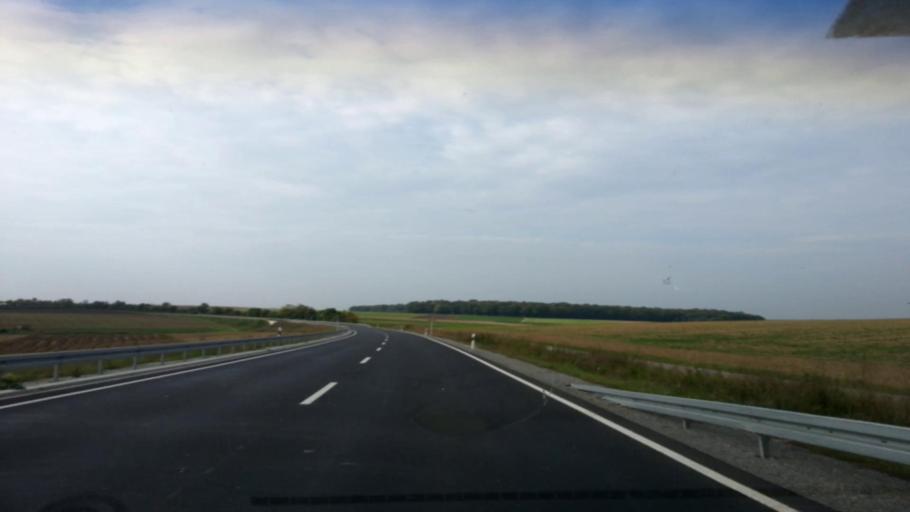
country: DE
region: Bavaria
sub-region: Regierungsbezirk Unterfranken
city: Lulsfeld
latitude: 49.8647
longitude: 10.3546
